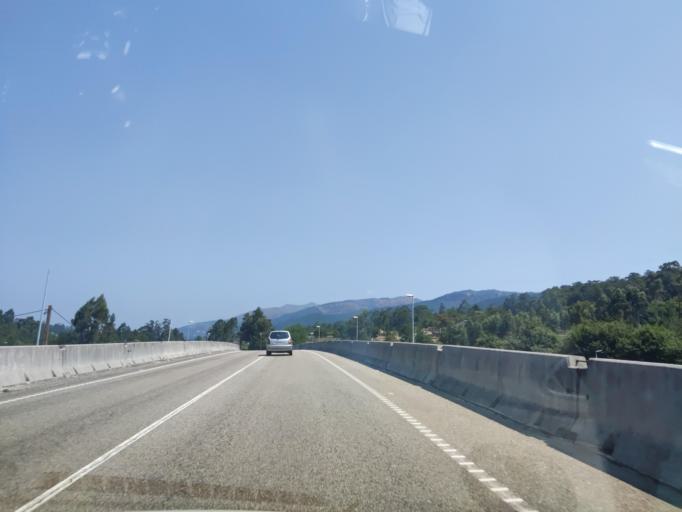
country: ES
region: Galicia
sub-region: Provincia de Pontevedra
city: Porrino
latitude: 42.1857
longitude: -8.6117
